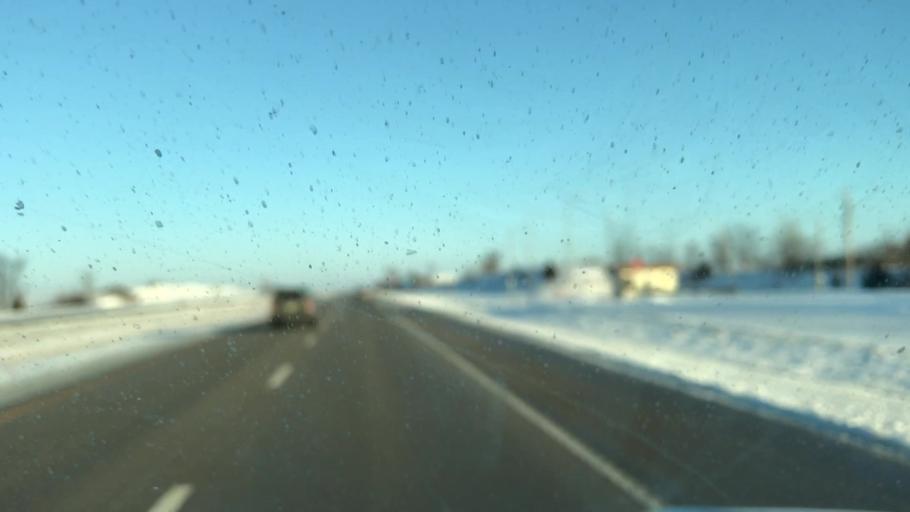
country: US
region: Missouri
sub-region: Andrew County
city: Country Club Village
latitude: 39.7475
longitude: -94.6960
